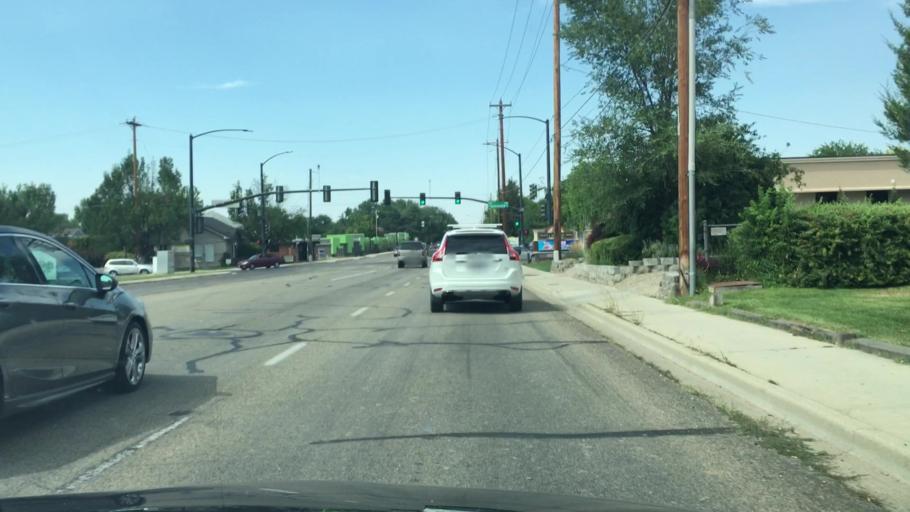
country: US
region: Idaho
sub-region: Ada County
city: Garden City
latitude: 43.6260
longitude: -116.2742
